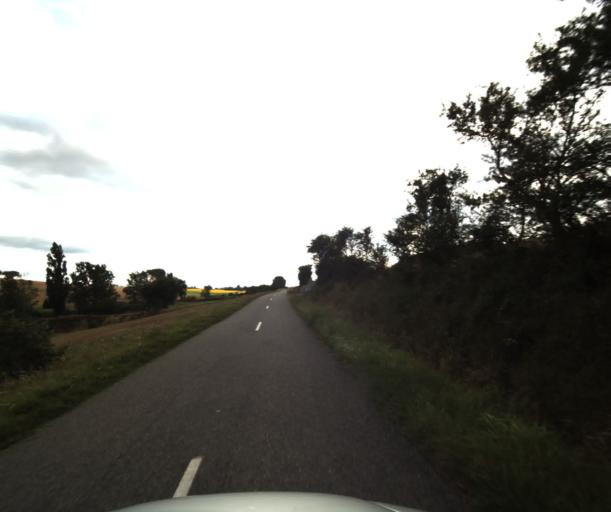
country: FR
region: Midi-Pyrenees
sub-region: Departement de la Haute-Garonne
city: Eaunes
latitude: 43.4107
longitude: 1.3302
